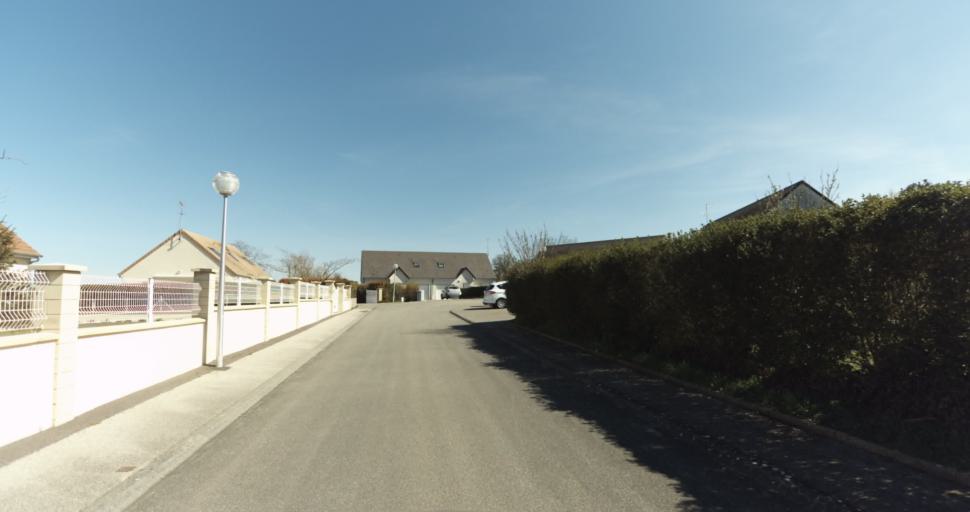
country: FR
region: Lower Normandy
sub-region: Departement du Calvados
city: Saint-Pierre-sur-Dives
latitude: 49.0380
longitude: -0.0164
